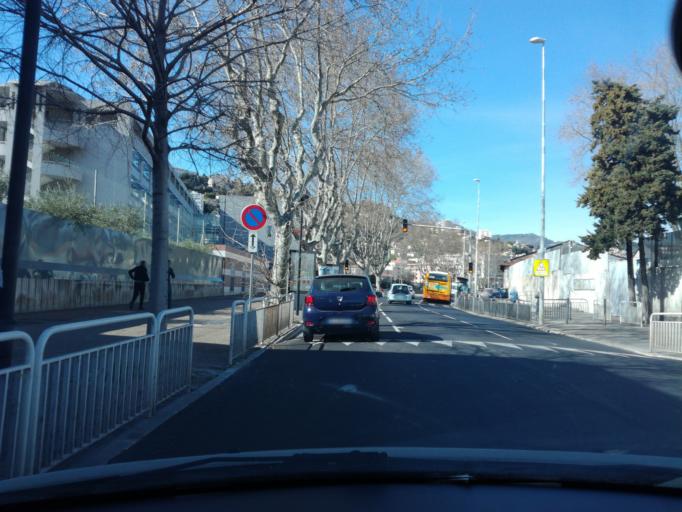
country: FR
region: Provence-Alpes-Cote d'Azur
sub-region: Departement des Alpes-Maritimes
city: Saint-Andre-de-la-Roche
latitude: 43.7147
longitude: 7.2831
